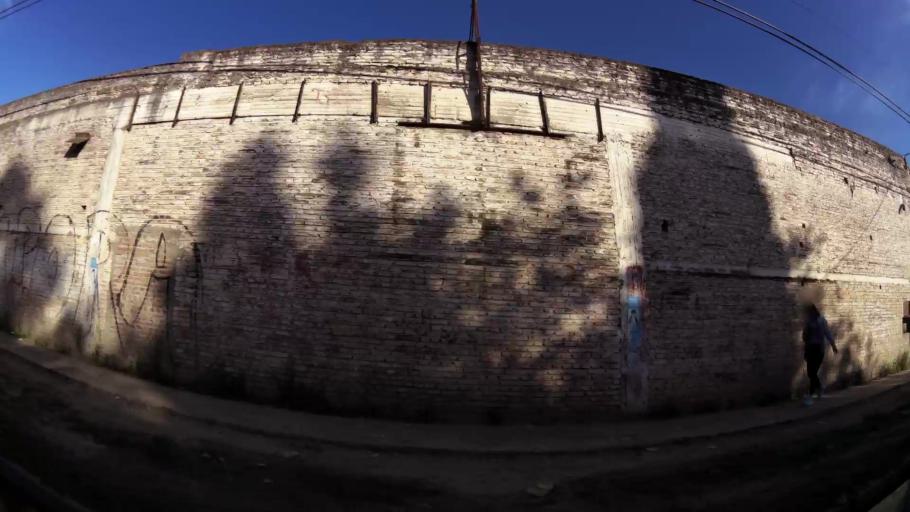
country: AR
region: Buenos Aires
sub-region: Partido de Quilmes
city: Quilmes
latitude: -34.8148
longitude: -58.2032
